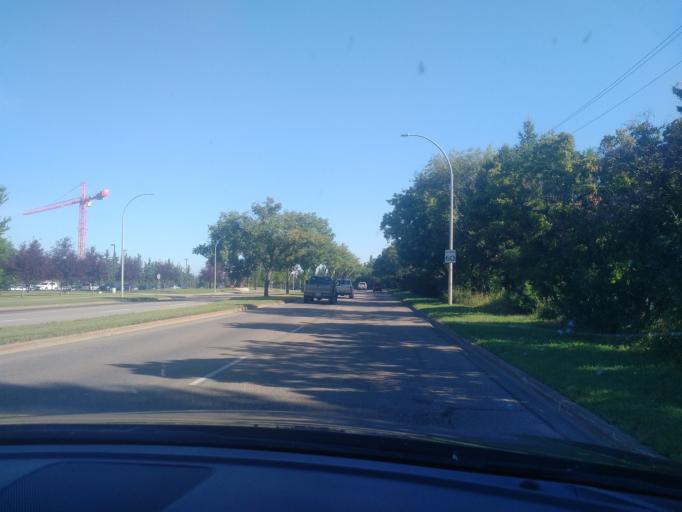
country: CA
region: Alberta
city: Edmonton
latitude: 53.5042
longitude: -113.5227
